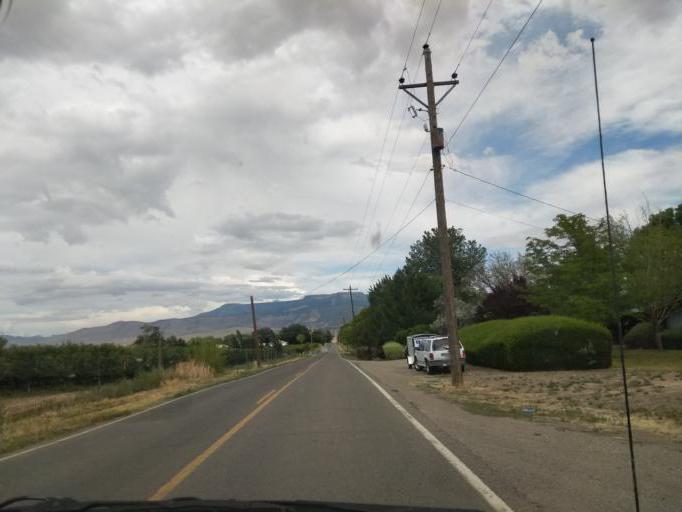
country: US
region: Colorado
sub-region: Mesa County
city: Clifton
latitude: 39.0558
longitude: -108.4335
